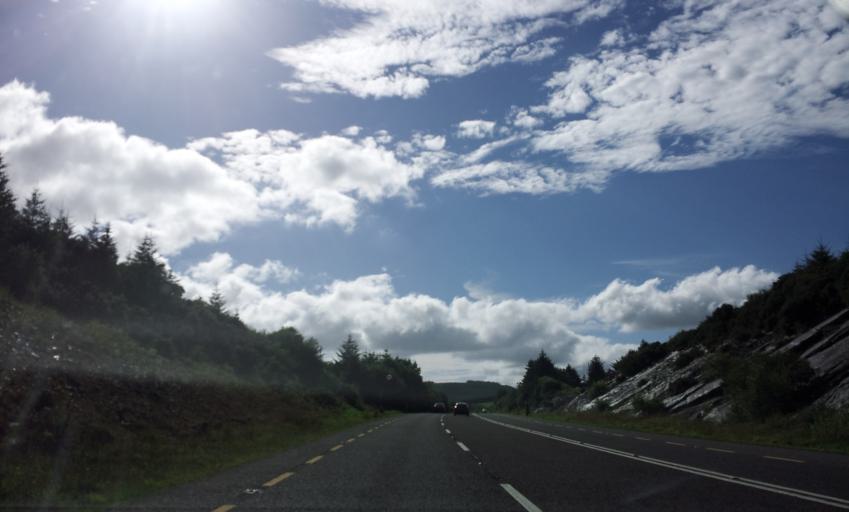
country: IE
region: Munster
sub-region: County Cork
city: Millstreet
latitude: 51.9623
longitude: -9.2162
